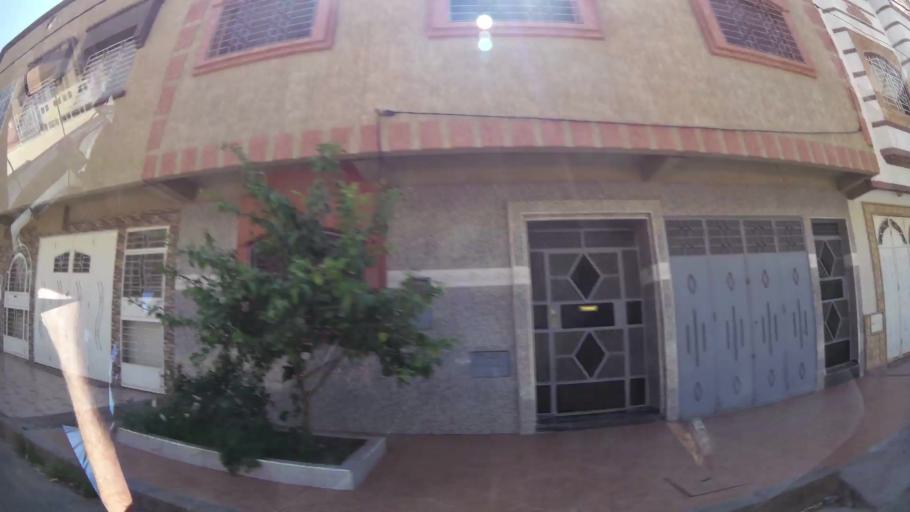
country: MA
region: Oriental
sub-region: Oujda-Angad
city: Oujda
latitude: 34.6950
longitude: -1.8824
